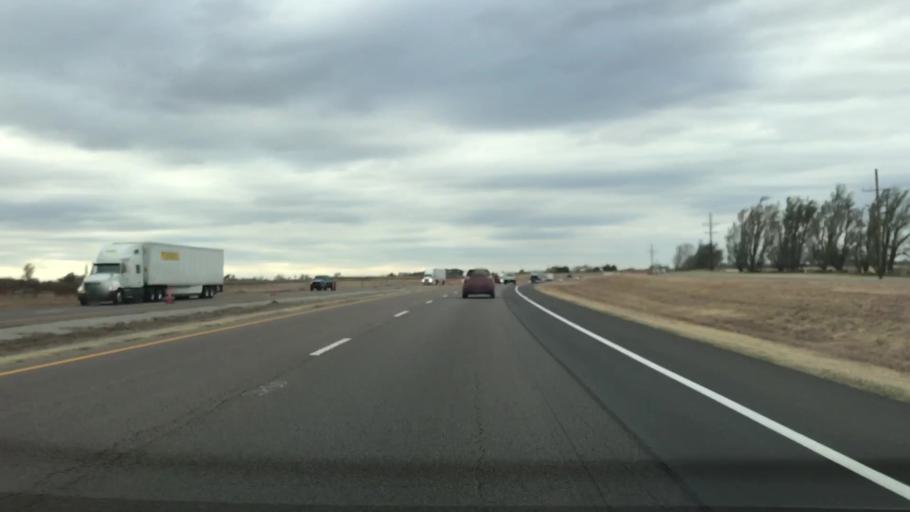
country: US
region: Oklahoma
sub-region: Beckham County
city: Elk City
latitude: 35.4225
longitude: -99.3012
